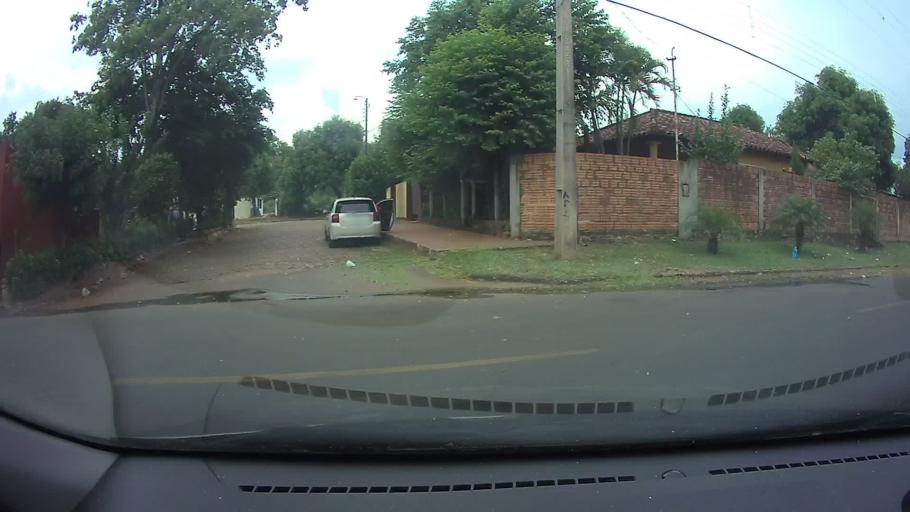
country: PY
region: Central
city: San Lorenzo
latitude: -25.2800
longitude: -57.4816
